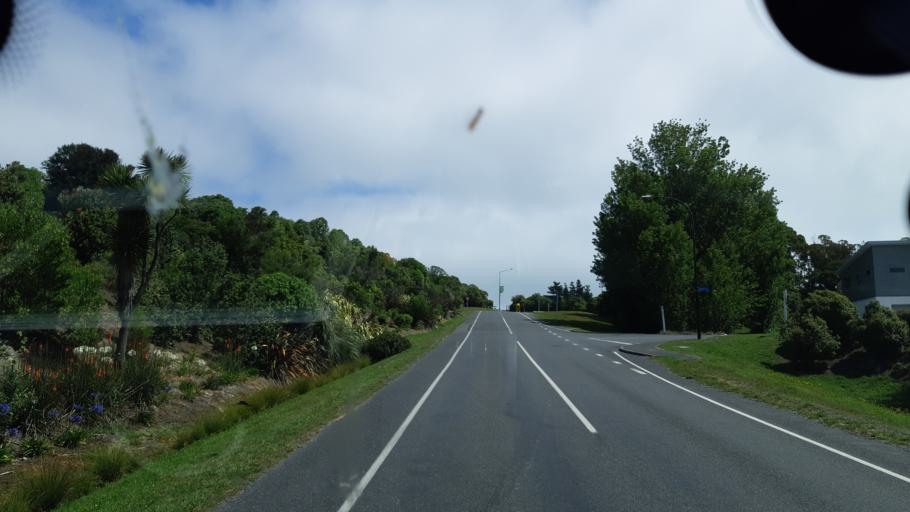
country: NZ
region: Canterbury
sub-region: Kaikoura District
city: Kaikoura
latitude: -42.4085
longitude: 173.6805
